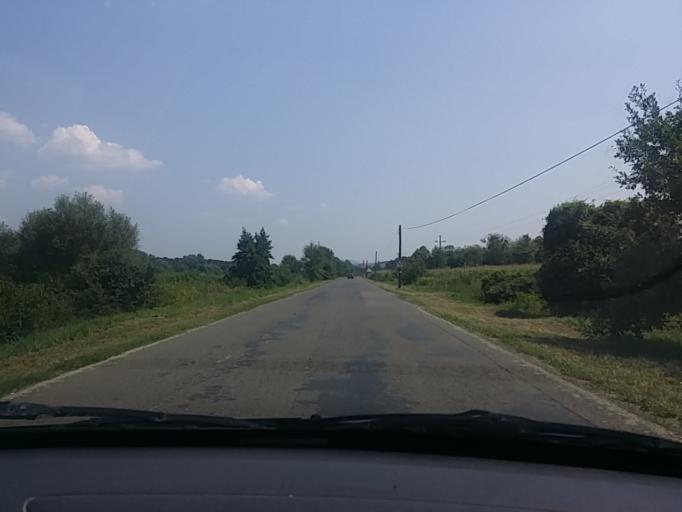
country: HU
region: Baranya
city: Sasd
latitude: 46.1937
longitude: 18.1376
